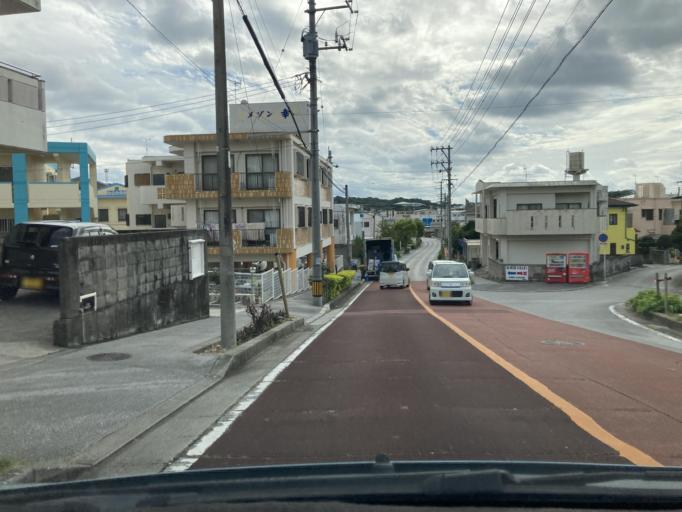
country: JP
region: Okinawa
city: Itoman
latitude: 26.1290
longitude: 127.6785
